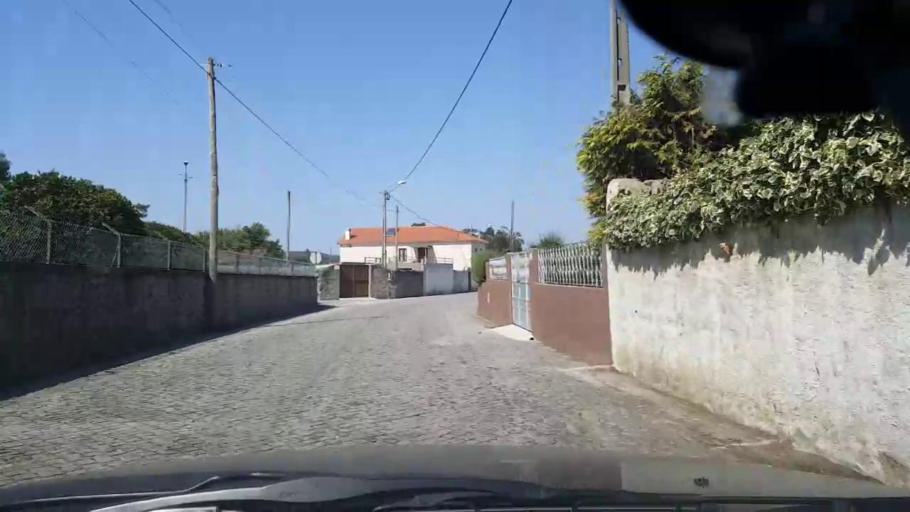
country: PT
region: Porto
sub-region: Vila do Conde
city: Arvore
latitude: 41.3819
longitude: -8.7034
